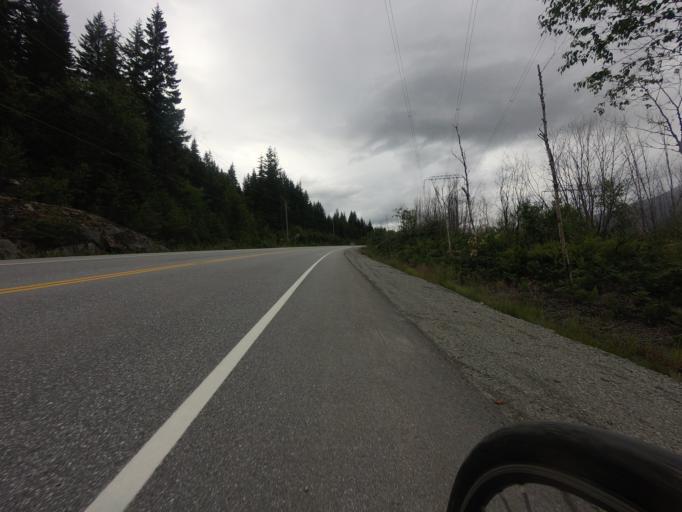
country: CA
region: British Columbia
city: Whistler
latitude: 50.1888
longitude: -122.8767
